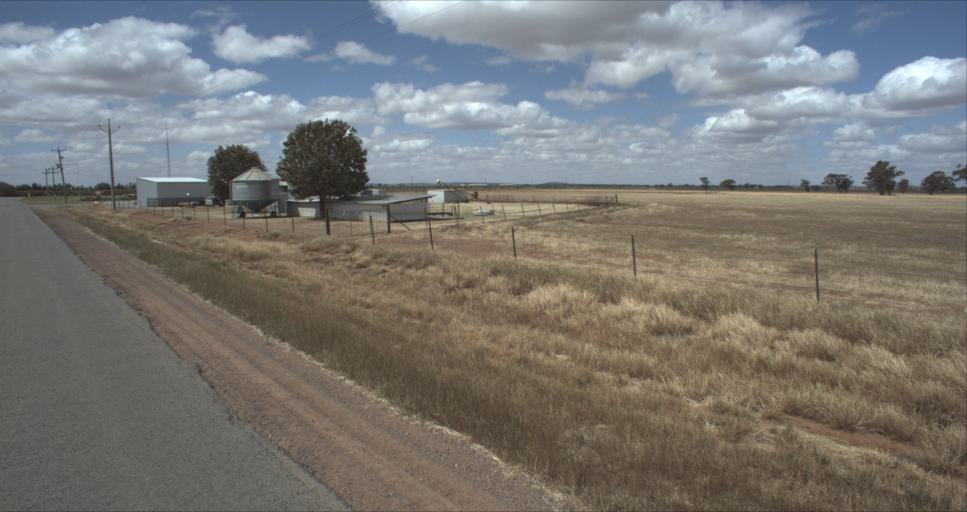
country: AU
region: New South Wales
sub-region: Leeton
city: Leeton
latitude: -34.5887
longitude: 146.3706
